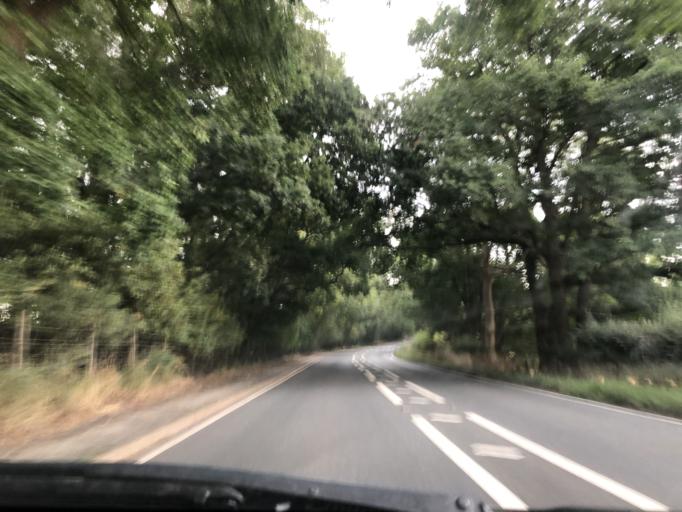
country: GB
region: England
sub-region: Kent
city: Sevenoaks
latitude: 51.2260
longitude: 0.2244
